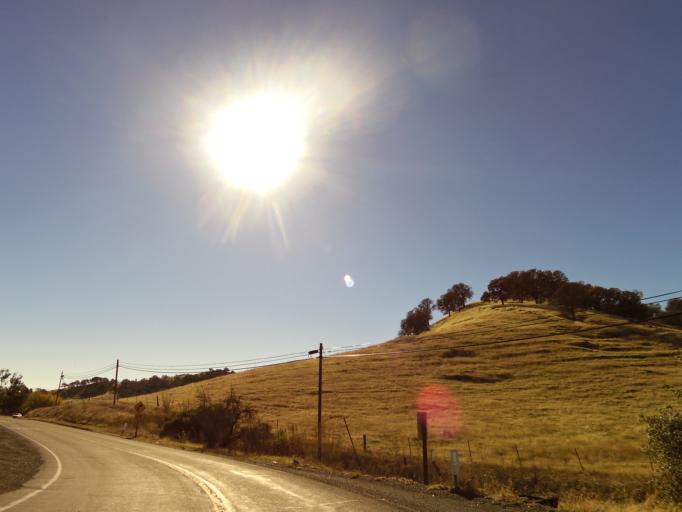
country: US
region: California
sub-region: Solano County
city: Vacaville
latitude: 38.3262
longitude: -122.0260
